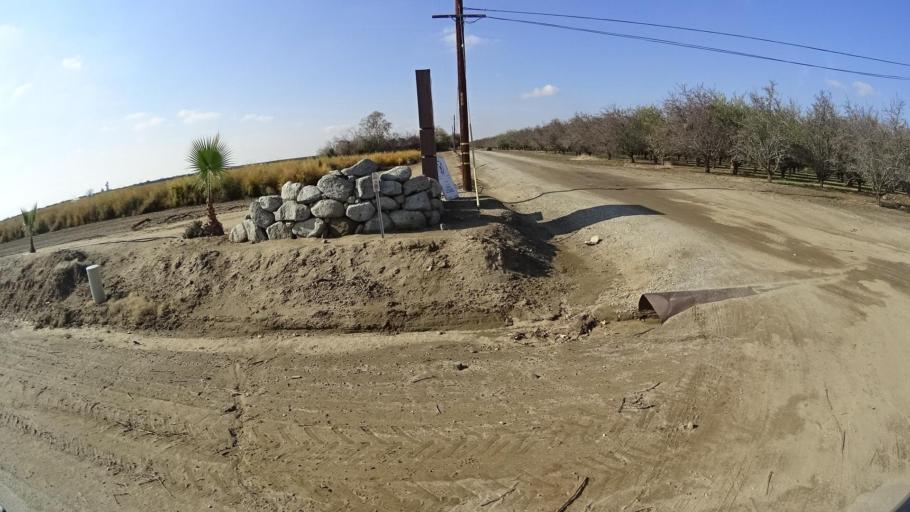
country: US
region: California
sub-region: Kern County
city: Arvin
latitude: 35.2312
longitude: -118.7884
